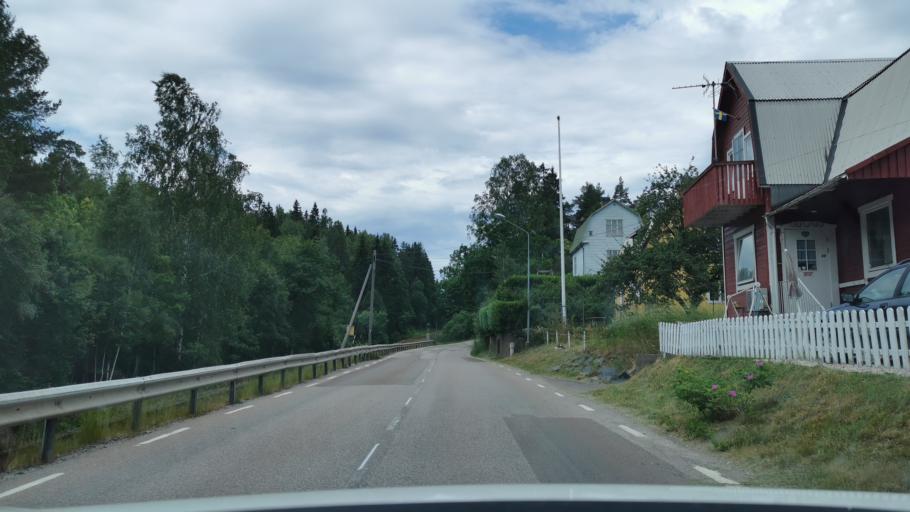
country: SE
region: Vaestra Goetaland
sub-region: Melleruds Kommun
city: Mellerud
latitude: 58.8278
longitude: 12.4131
